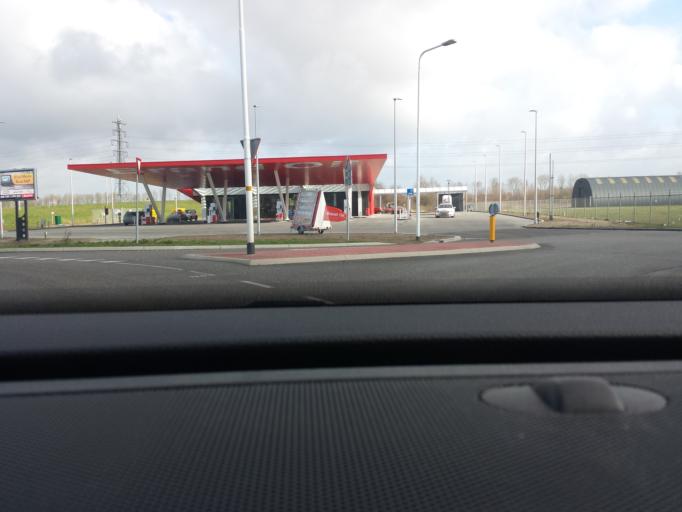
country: NL
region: Gelderland
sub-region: Gemeente Zutphen
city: Zutphen
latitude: 52.1583
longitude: 6.2027
